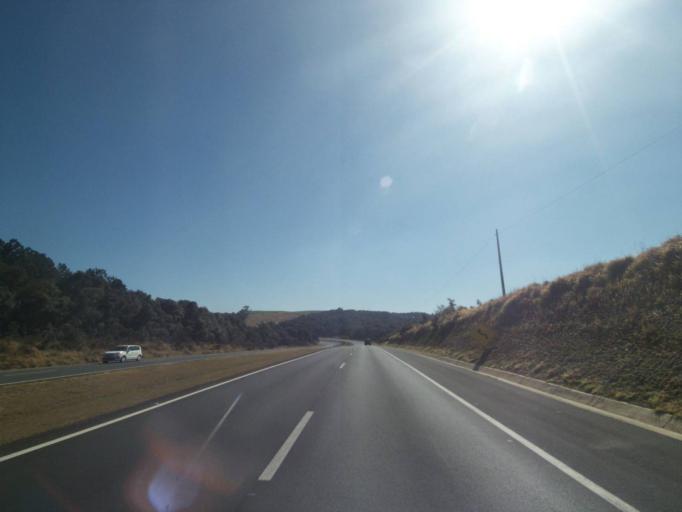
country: BR
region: Parana
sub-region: Carambei
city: Carambei
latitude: -24.8805
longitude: -50.4394
